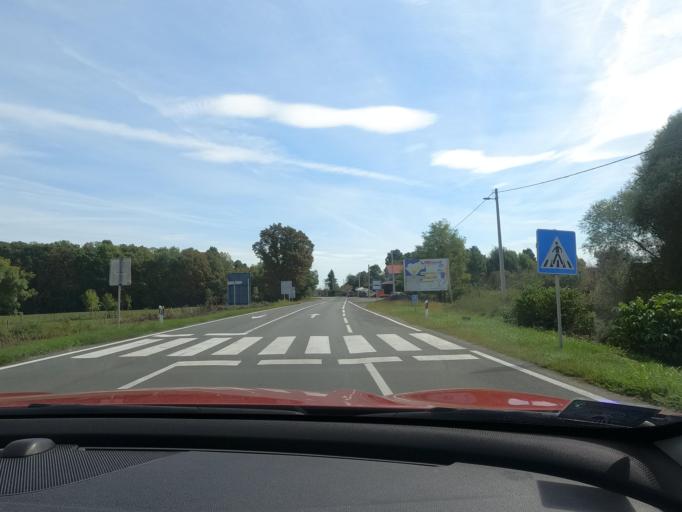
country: HR
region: Sisacko-Moslavacka
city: Budasevo
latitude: 45.4858
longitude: 16.4681
